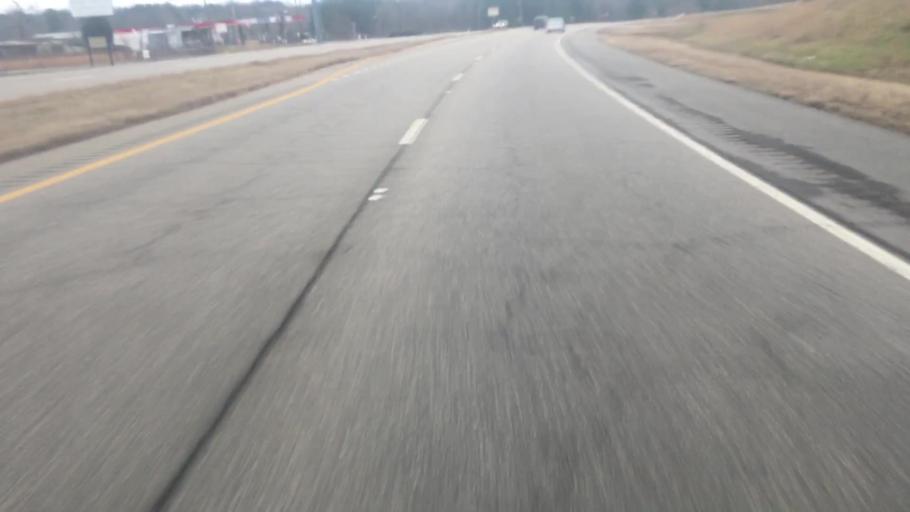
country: US
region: Alabama
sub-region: Walker County
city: Cordova
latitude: 33.8207
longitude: -87.1548
